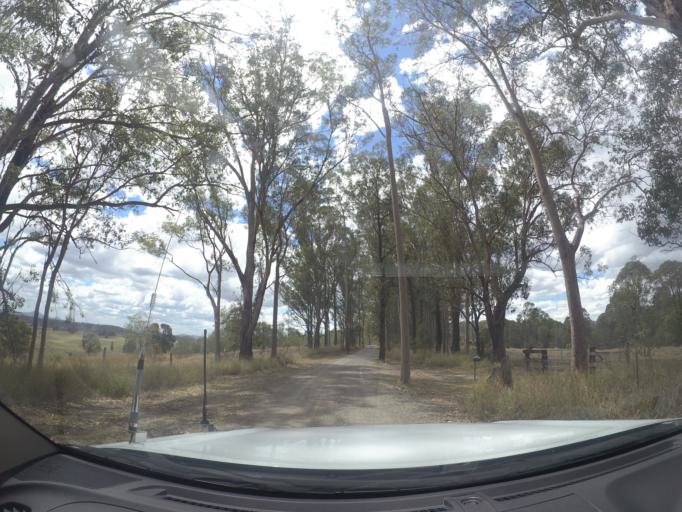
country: AU
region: Queensland
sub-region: Logan
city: Cedar Vale
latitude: -27.9144
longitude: 153.0310
